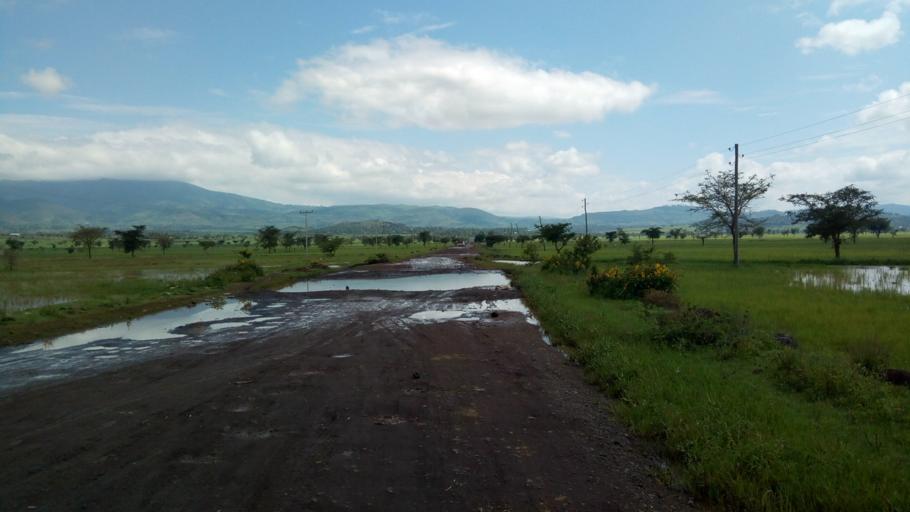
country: ET
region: Oromiya
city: Bishoftu
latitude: 8.8045
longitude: 39.0034
